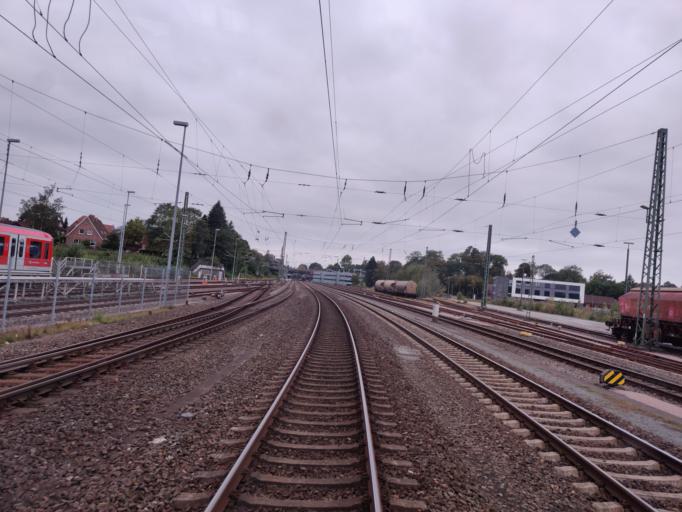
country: DE
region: Lower Saxony
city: Stade
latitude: 53.5950
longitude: 9.4844
